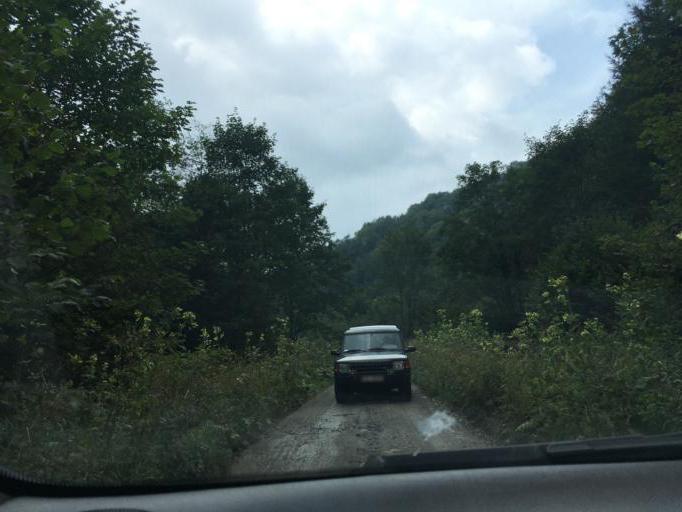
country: PL
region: Subcarpathian Voivodeship
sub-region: Powiat bieszczadzki
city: Lutowiska
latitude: 49.1836
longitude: 22.6171
